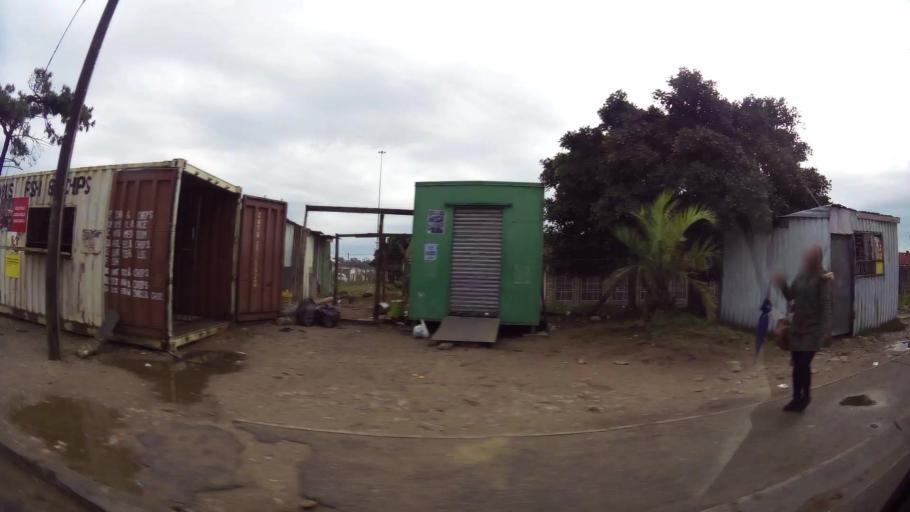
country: ZA
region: Eastern Cape
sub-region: Nelson Mandela Bay Metropolitan Municipality
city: Port Elizabeth
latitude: -33.9906
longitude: 25.5870
